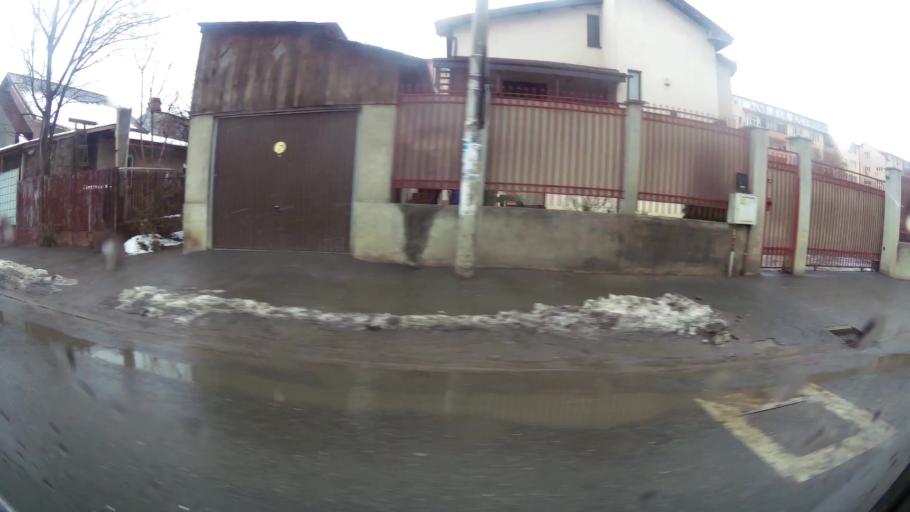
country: RO
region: Ilfov
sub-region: Comuna Chiajna
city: Rosu
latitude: 44.4103
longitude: 26.0203
